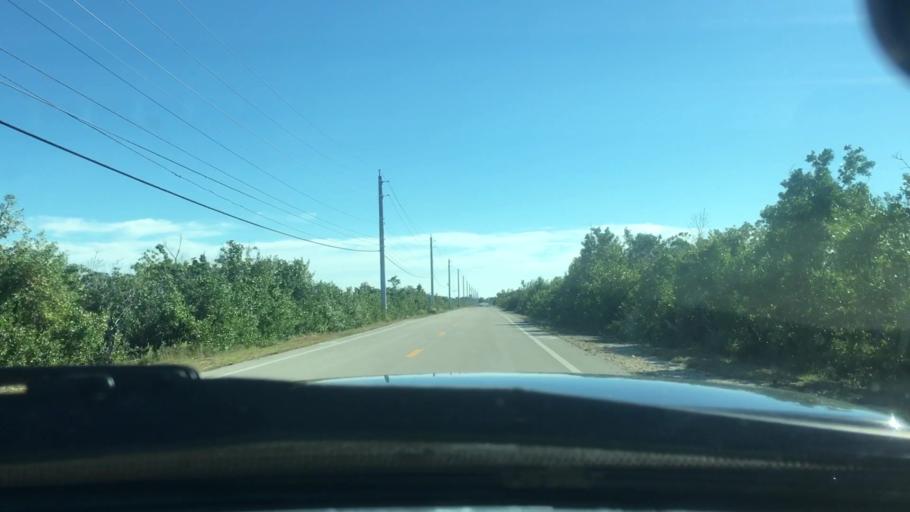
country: US
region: Florida
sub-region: Monroe County
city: Cudjoe Key
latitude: 24.6770
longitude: -81.4997
